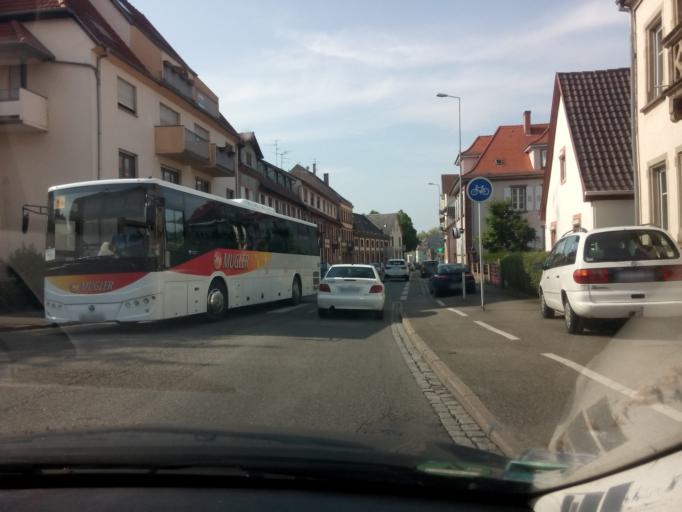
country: FR
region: Alsace
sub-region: Departement du Bas-Rhin
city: Haguenau
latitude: 48.8106
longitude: 7.7959
